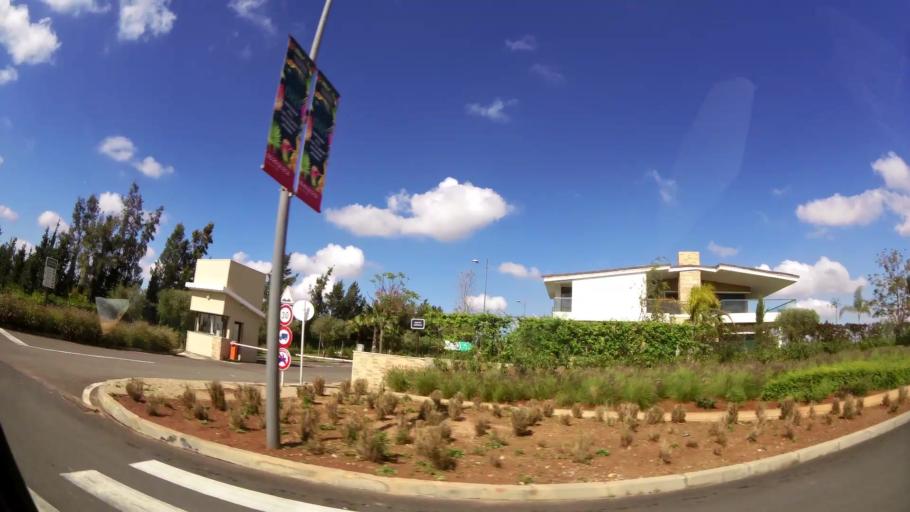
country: MA
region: Grand Casablanca
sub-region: Nouaceur
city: Bouskoura
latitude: 33.4756
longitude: -7.6024
